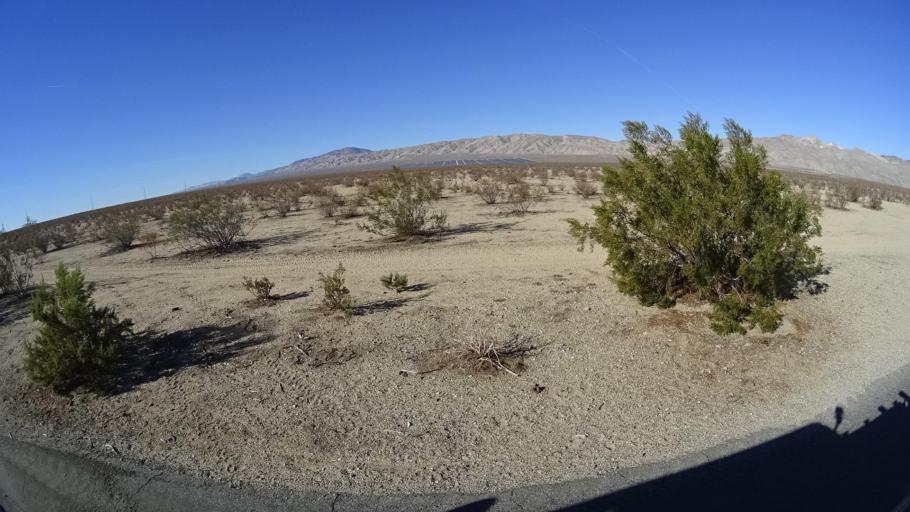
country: US
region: California
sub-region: Kern County
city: California City
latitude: 35.2056
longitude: -118.0212
